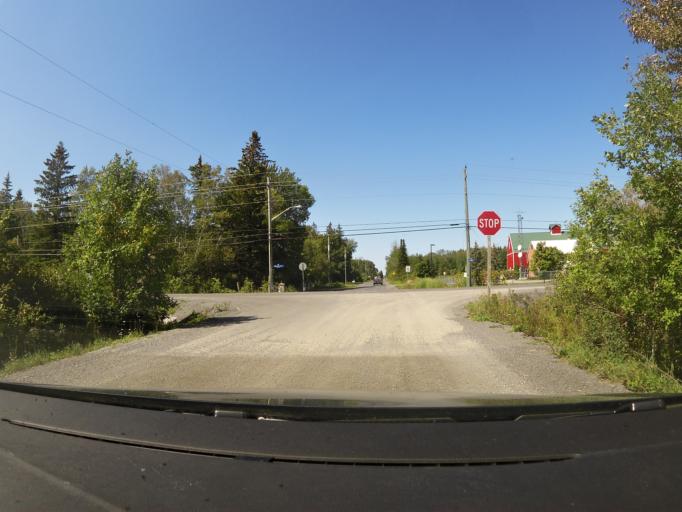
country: CA
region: Ontario
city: Bells Corners
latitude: 45.2848
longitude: -75.9847
